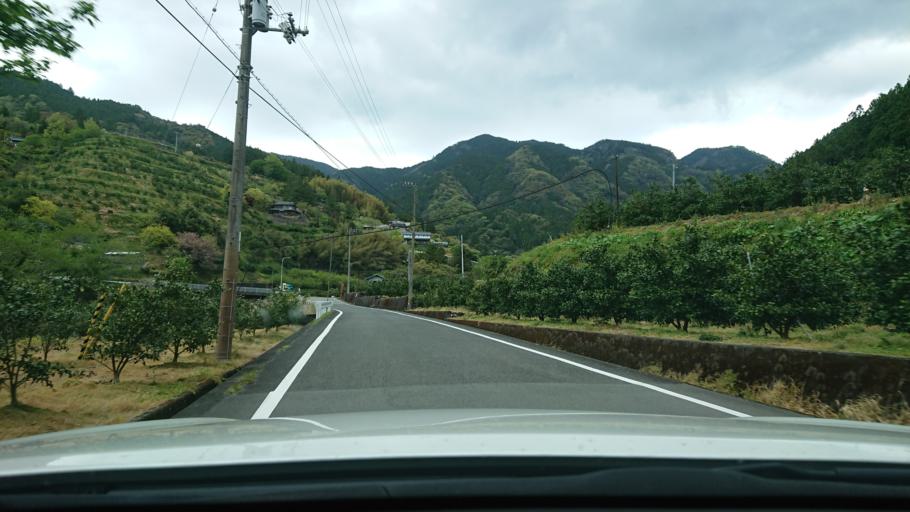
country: JP
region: Tokushima
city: Ishii
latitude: 33.9248
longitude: 134.4238
